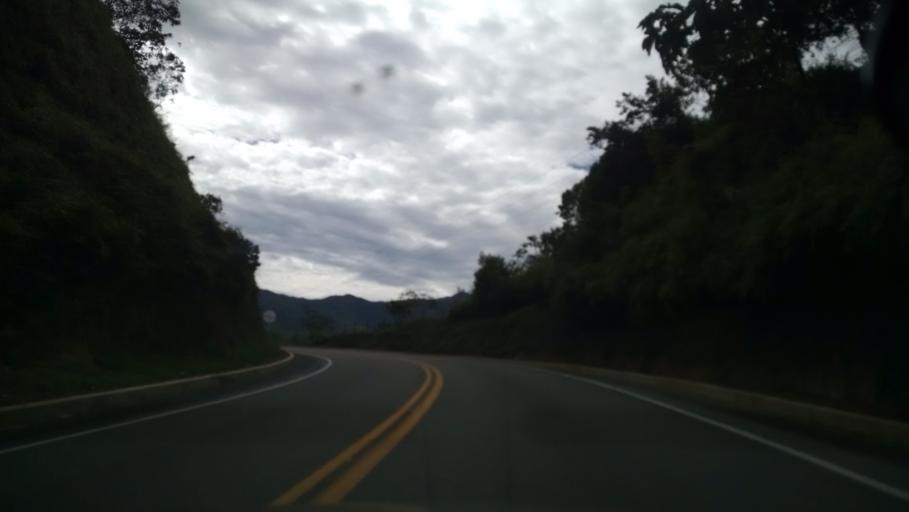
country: CO
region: Antioquia
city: Cocorna
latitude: 6.0286
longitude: -75.1730
